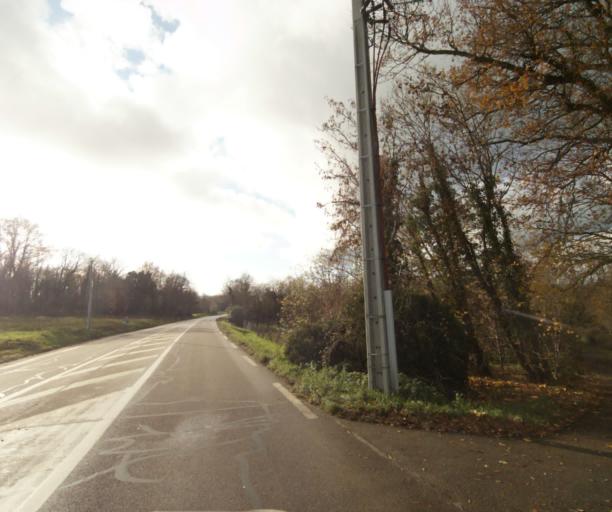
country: FR
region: Ile-de-France
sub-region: Departement des Yvelines
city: Vaux-sur-Seine
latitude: 49.0151
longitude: 1.9387
